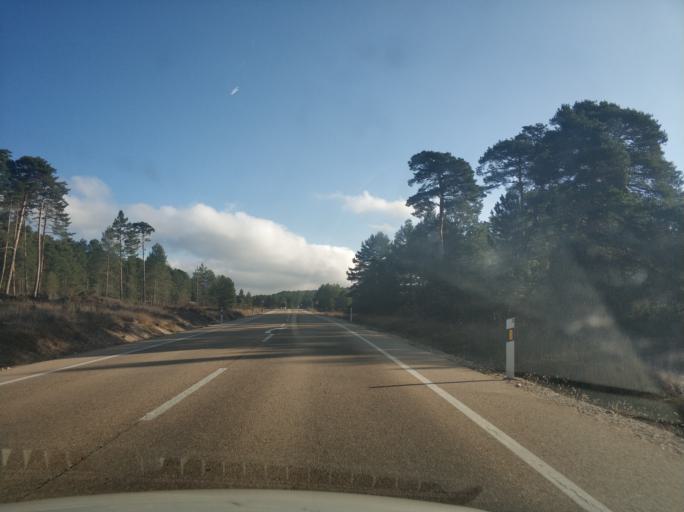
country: ES
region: Castille and Leon
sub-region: Provincia de Soria
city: San Leonardo de Yague
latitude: 41.8365
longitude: -3.0371
